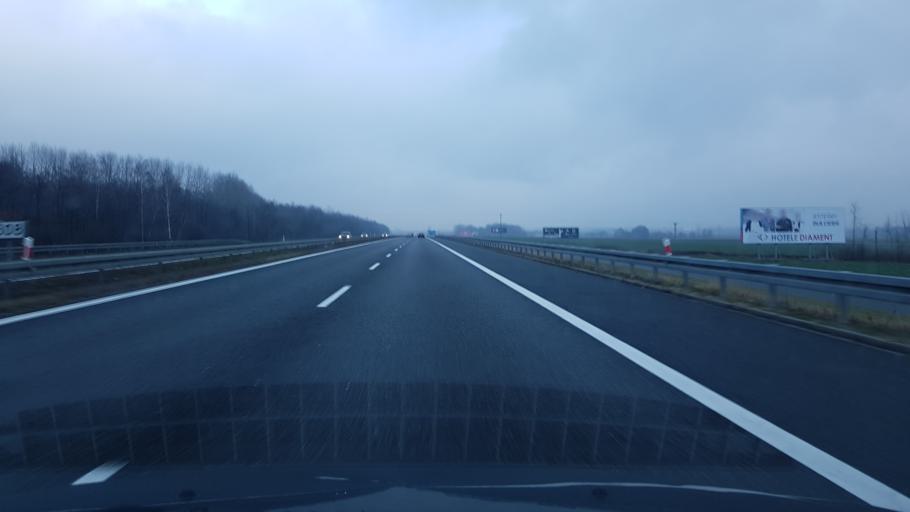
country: PL
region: Silesian Voivodeship
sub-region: Powiat gliwicki
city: Zernica
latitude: 50.2641
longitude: 18.6127
